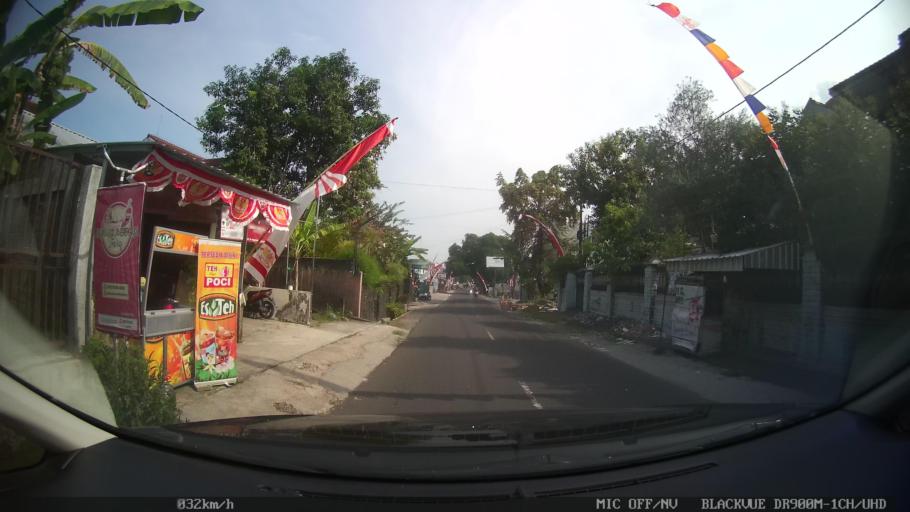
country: ID
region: Daerah Istimewa Yogyakarta
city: Depok
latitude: -7.7671
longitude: 110.4247
